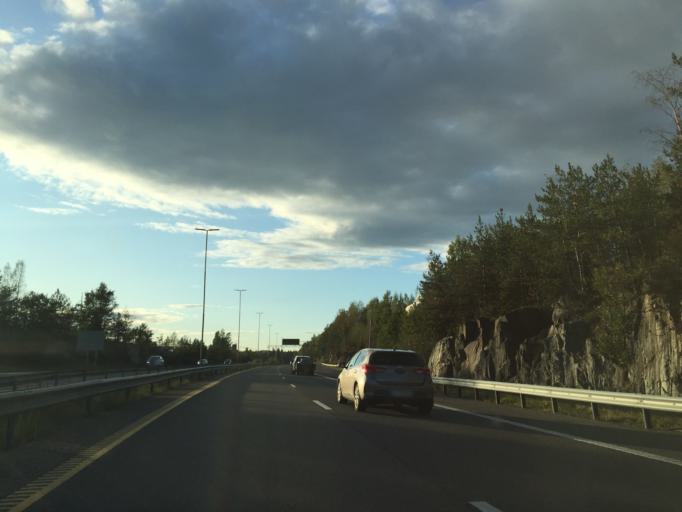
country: NO
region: Akershus
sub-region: Lorenskog
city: Kjenn
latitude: 59.9317
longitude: 10.9446
